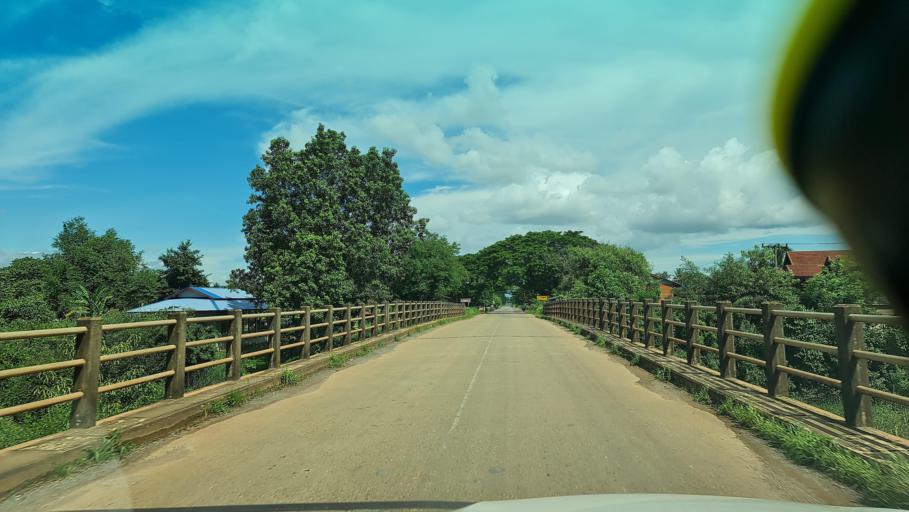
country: LA
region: Bolikhamxai
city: Ban Nahin
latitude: 18.2246
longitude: 104.1976
